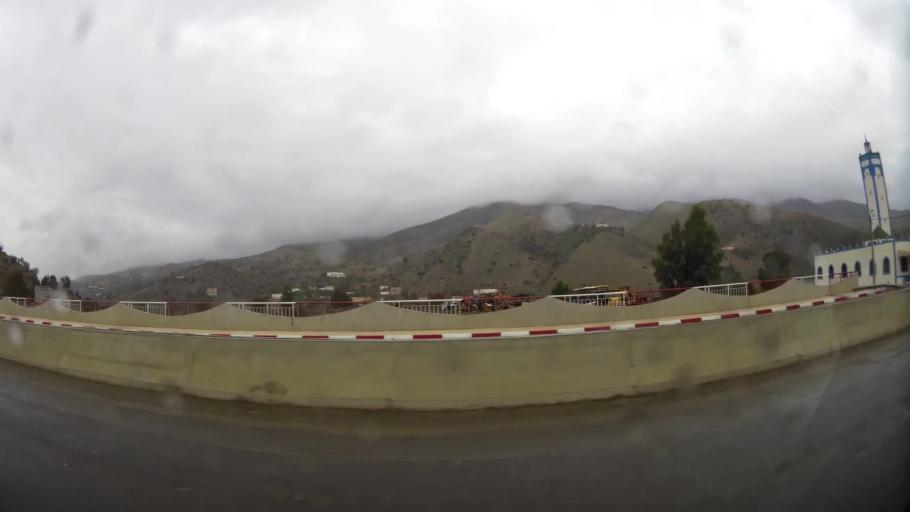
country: MA
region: Taza-Al Hoceima-Taounate
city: Imzourene
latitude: 35.0185
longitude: -3.8204
